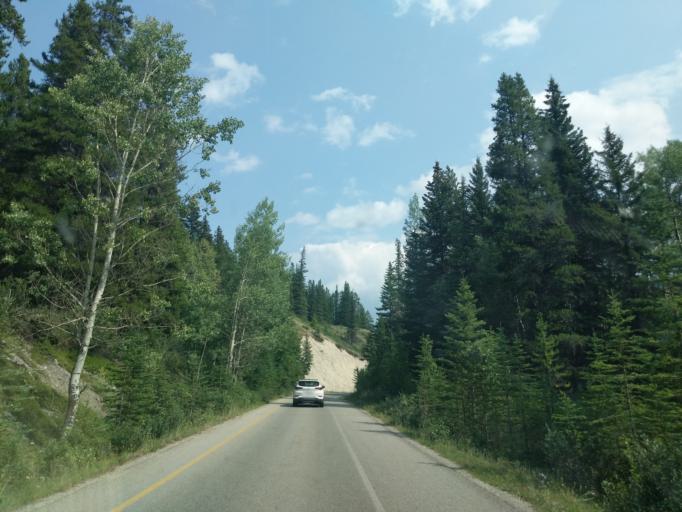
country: CA
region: Alberta
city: Banff
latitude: 51.1713
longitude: -115.7025
